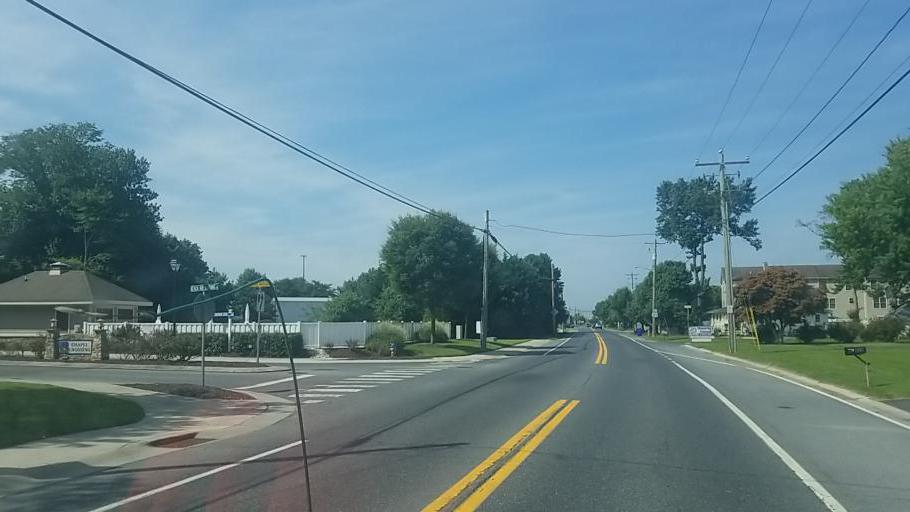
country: US
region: Delaware
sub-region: Sussex County
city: Millsboro
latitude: 38.5445
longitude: -75.2549
